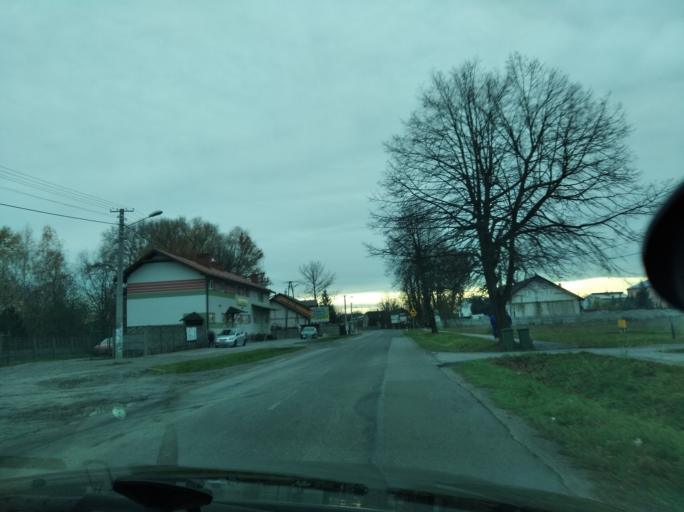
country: PL
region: Subcarpathian Voivodeship
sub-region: Powiat lancucki
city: Czarna
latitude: 50.0934
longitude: 22.1846
